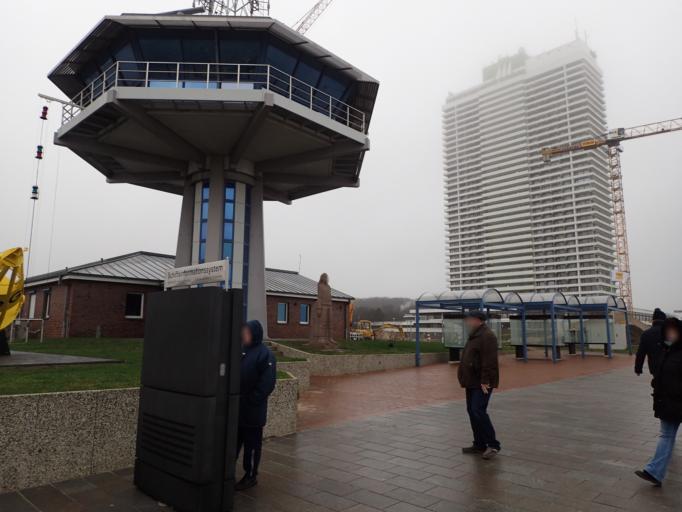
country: DE
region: Schleswig-Holstein
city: Travemuende
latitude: 53.9608
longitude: 10.8833
